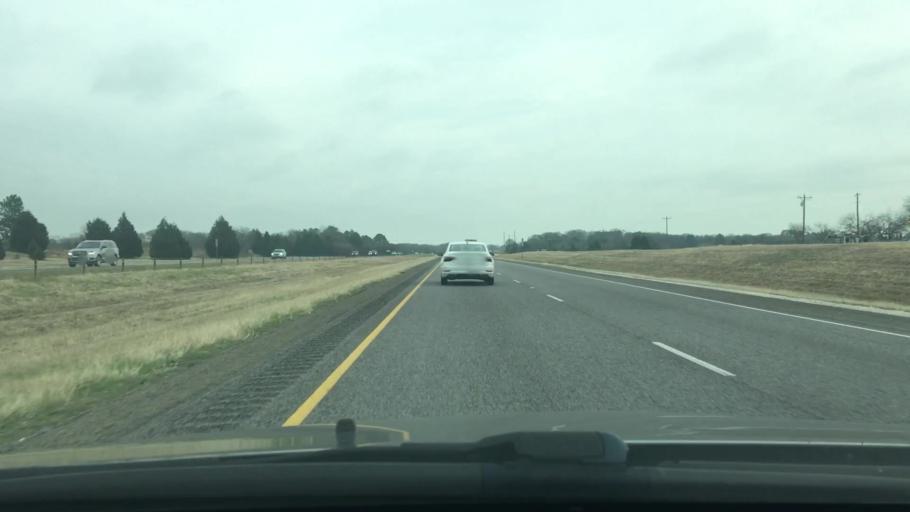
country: US
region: Texas
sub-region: Freestone County
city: Fairfield
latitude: 31.7414
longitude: -96.1913
